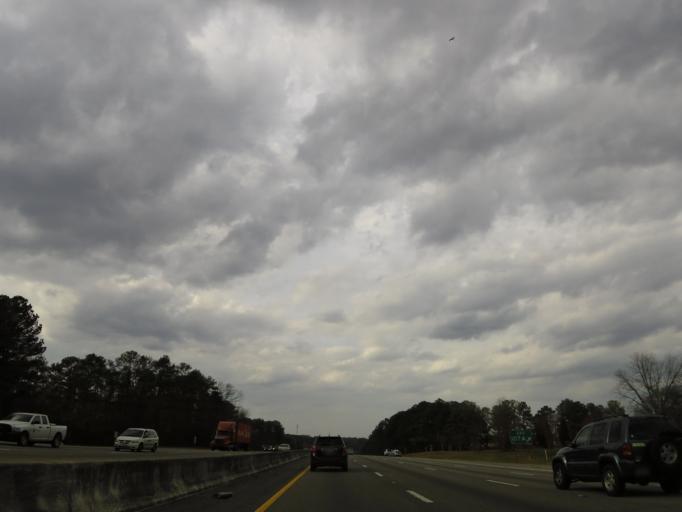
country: US
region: South Carolina
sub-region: Lexington County
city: Saint Andrews
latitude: 34.0376
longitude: -81.1112
